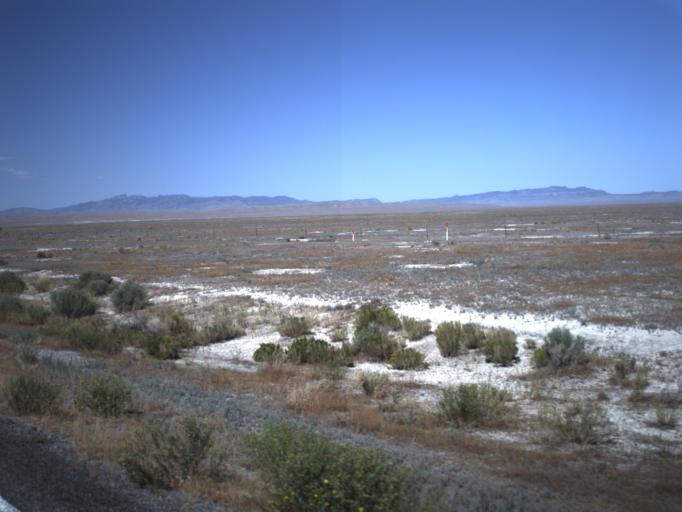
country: US
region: Utah
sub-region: Millard County
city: Delta
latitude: 39.2292
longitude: -112.9338
